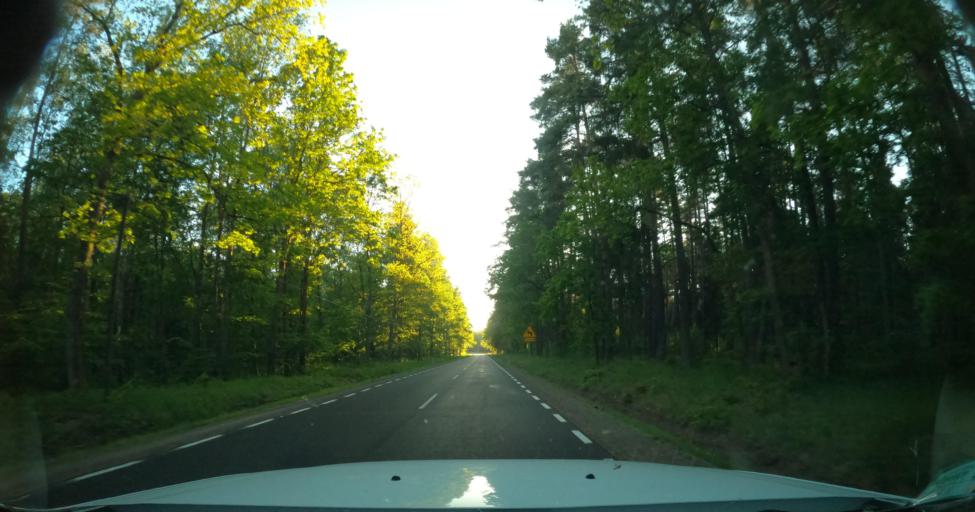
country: PL
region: Pomeranian Voivodeship
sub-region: Powiat bytowski
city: Czarna Dabrowka
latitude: 54.3428
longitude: 17.6029
